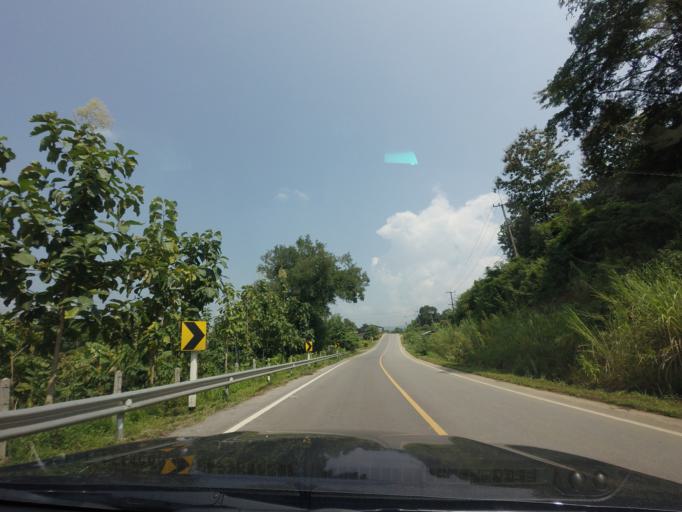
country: TH
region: Nan
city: Nan
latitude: 18.8687
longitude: 100.8313
